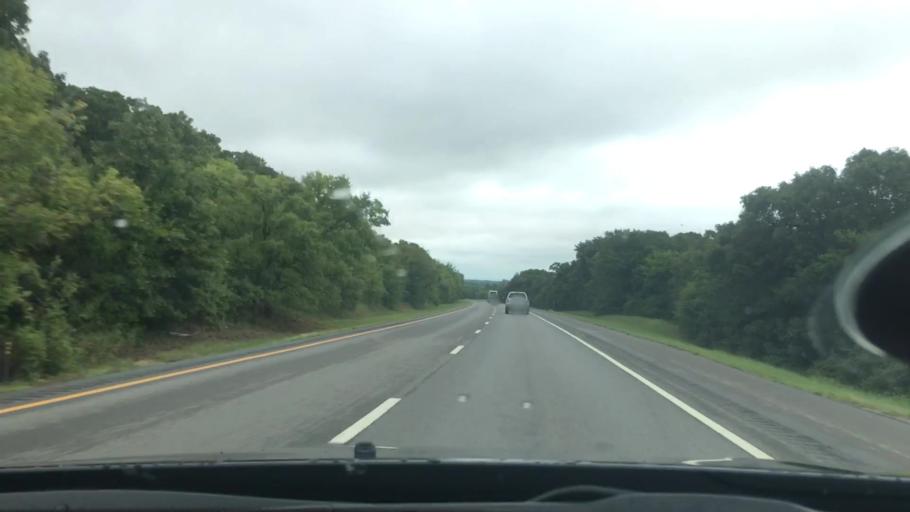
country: US
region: Oklahoma
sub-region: Okmulgee County
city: Morris
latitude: 35.4430
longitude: -95.7750
